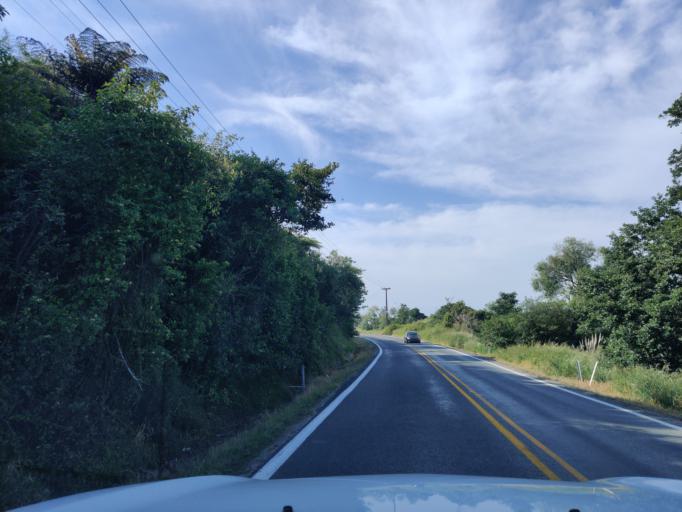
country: NZ
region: Waikato
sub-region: Waikato District
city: Ngaruawahia
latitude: -37.5939
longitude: 175.1558
